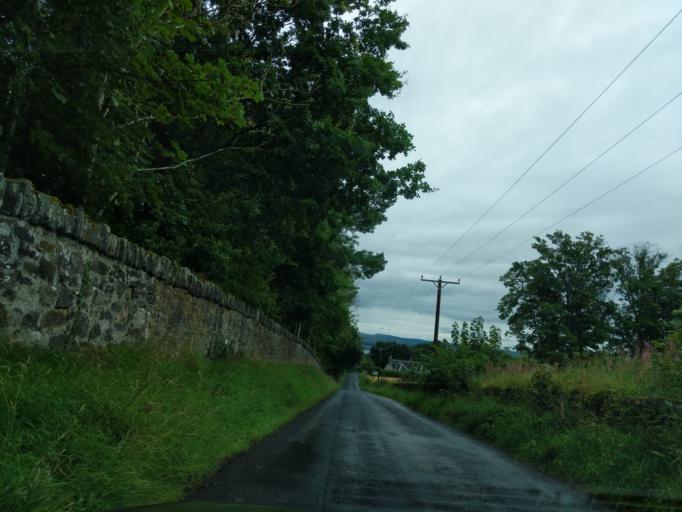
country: GB
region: Scotland
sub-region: Fife
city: Limekilns
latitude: 55.9860
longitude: -3.4648
